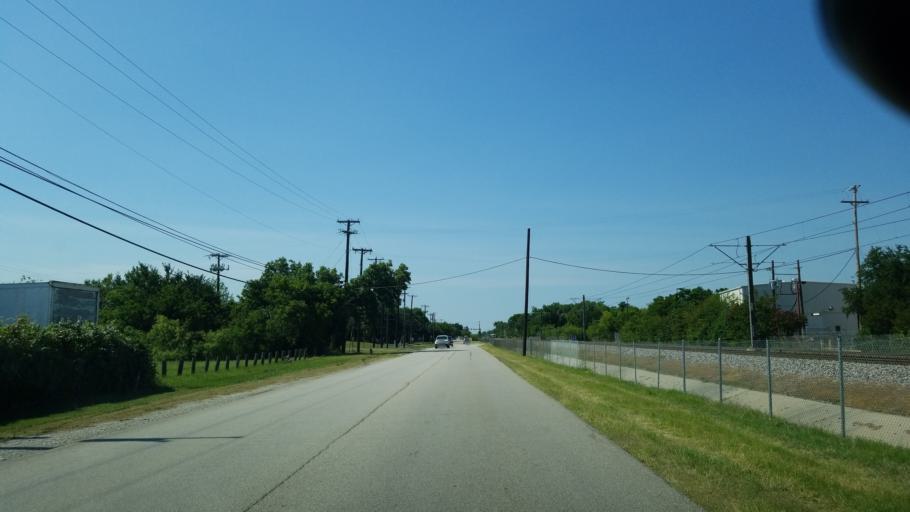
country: US
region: Texas
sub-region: Dallas County
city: Farmers Branch
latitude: 32.9137
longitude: -96.8939
